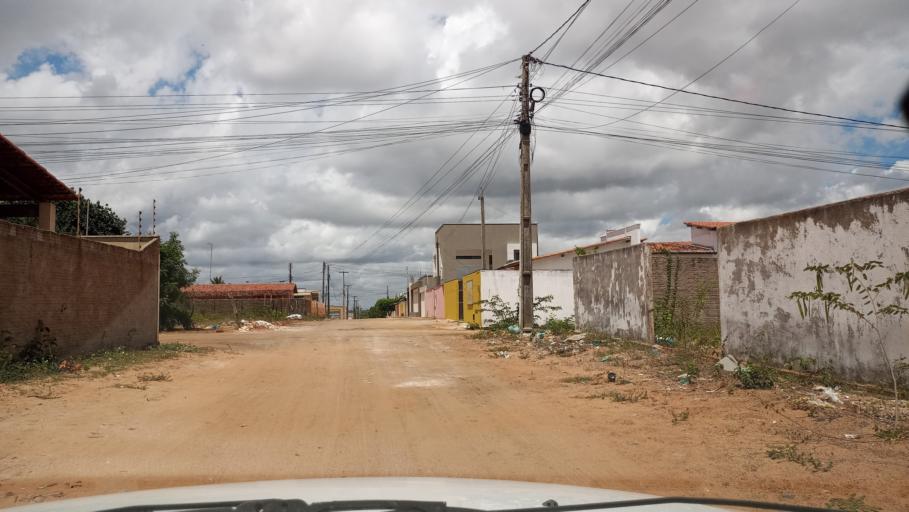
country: BR
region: Rio Grande do Norte
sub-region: Joao Camara
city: Joao Camara
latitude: -5.5286
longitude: -35.8084
